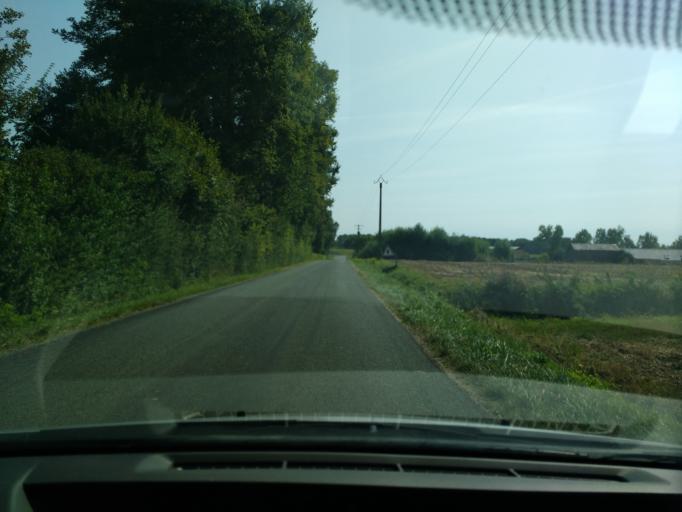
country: FR
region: Pays de la Loire
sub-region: Departement de Maine-et-Loire
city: Jarze
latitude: 47.5128
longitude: -0.2025
